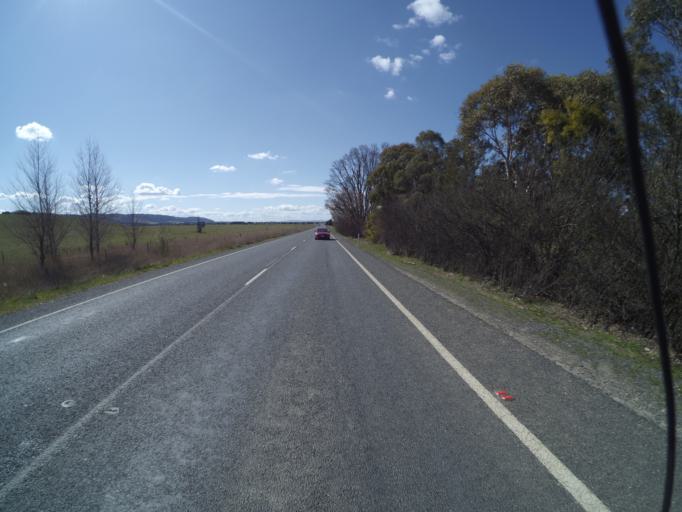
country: AU
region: New South Wales
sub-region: Palerang
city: Bungendore
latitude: -35.2860
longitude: 149.4212
